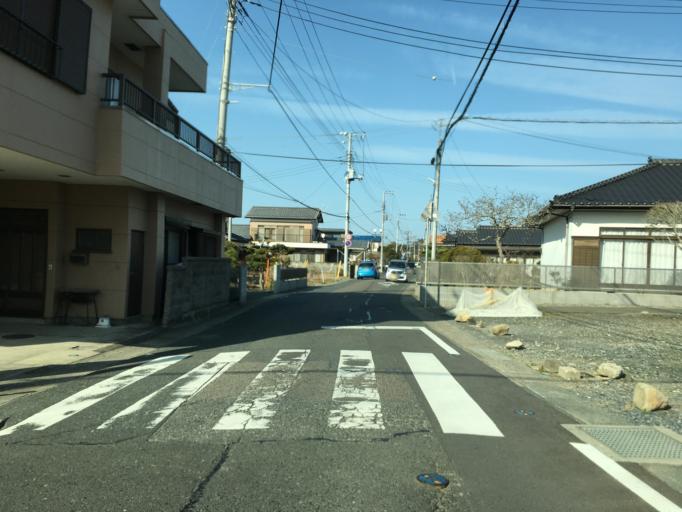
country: JP
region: Ibaraki
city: Kitaibaraki
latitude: 36.7528
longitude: 140.7309
